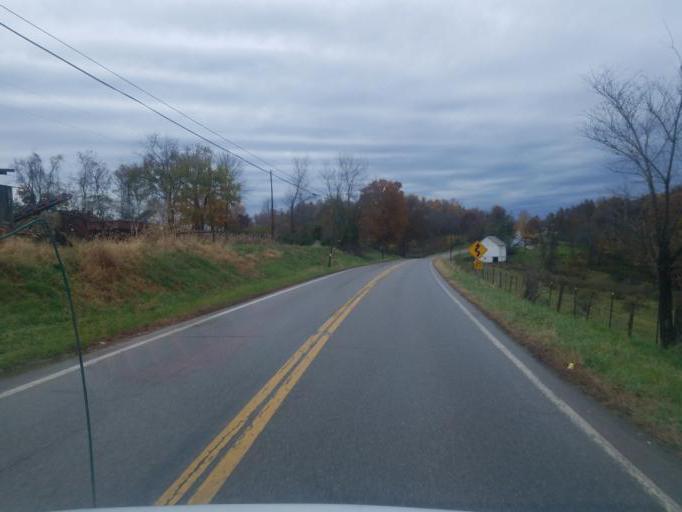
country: US
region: Ohio
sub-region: Morgan County
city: McConnelsville
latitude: 39.5189
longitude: -81.8506
